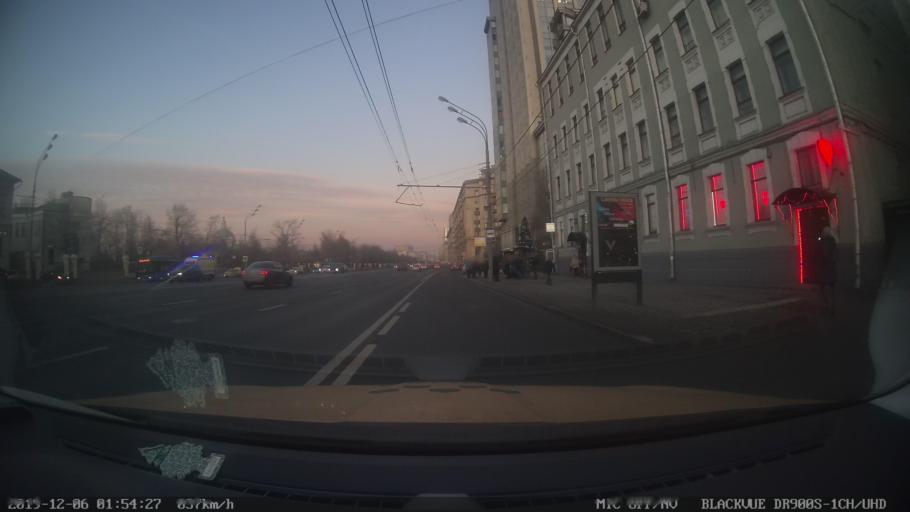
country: RU
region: Moscow
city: Novyye Cheremushki
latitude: 55.7208
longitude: 37.5987
